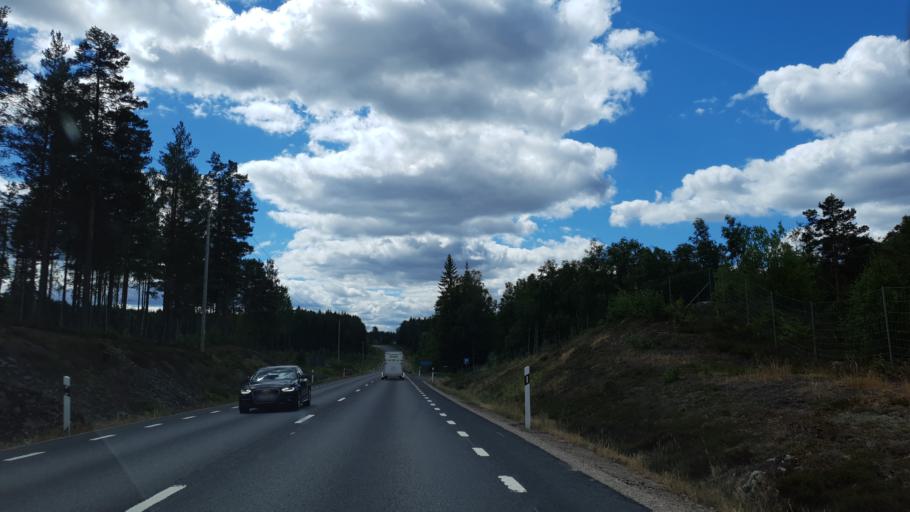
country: SE
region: Kronoberg
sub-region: Vaxjo Kommun
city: Braas
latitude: 57.1881
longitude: 15.1565
